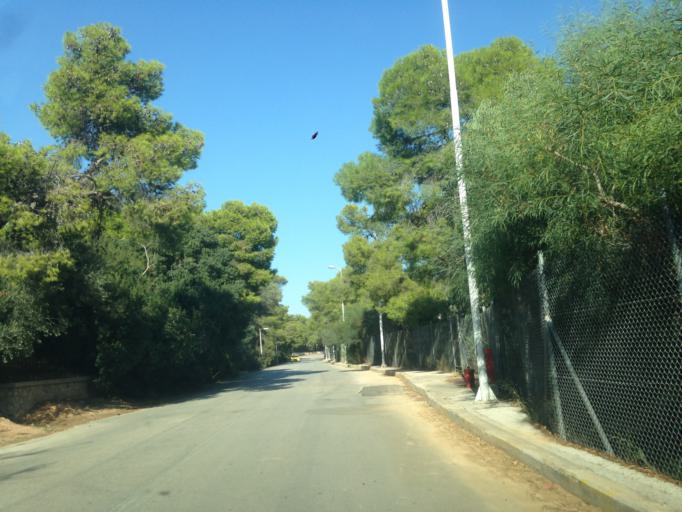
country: GR
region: Attica
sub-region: Nomarchia Anatolikis Attikis
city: Vouliagmeni
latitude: 37.8029
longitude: 23.7714
